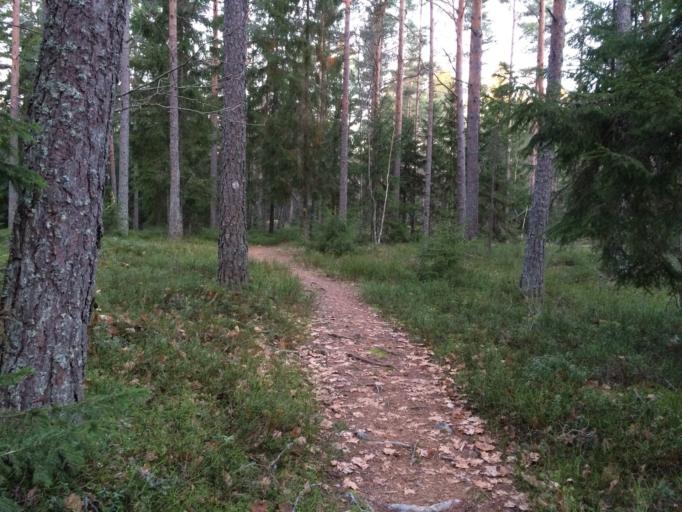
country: SE
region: Vaestmanland
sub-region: Hallstahammars Kommun
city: Hallstahammar
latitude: 59.6234
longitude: 16.1912
